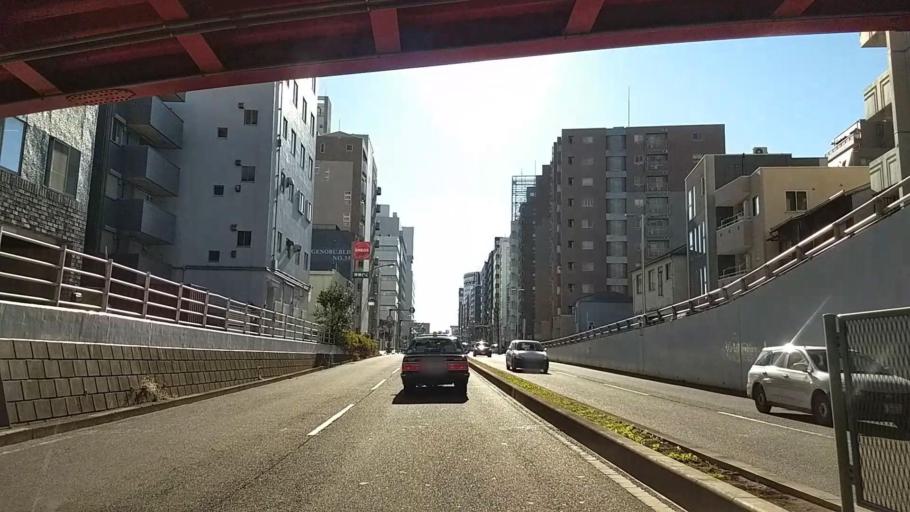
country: JP
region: Kanagawa
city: Yokohama
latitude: 35.4523
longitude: 139.6286
